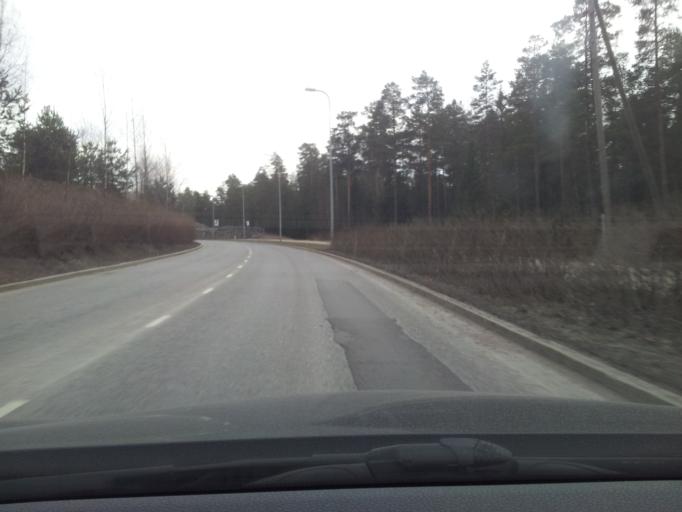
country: FI
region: Uusimaa
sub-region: Helsinki
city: Espoo
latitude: 60.1605
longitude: 24.6589
